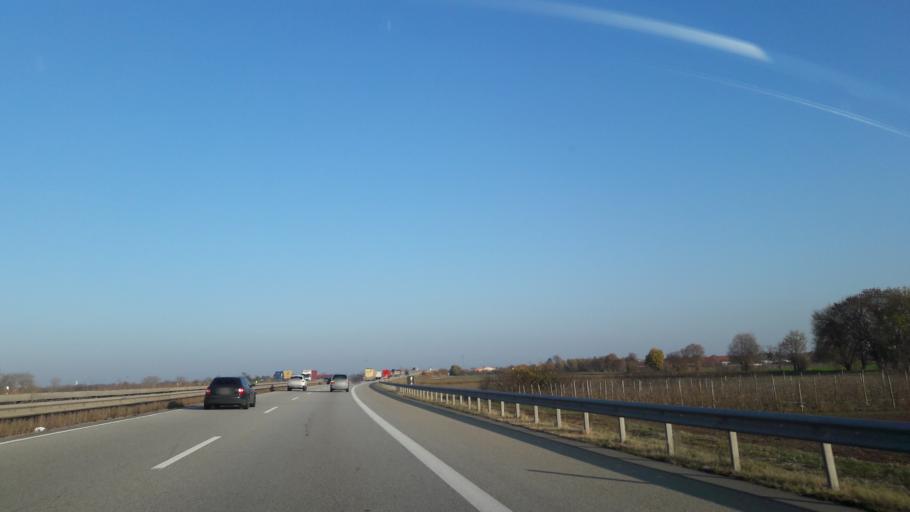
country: DE
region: Rheinland-Pfalz
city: Dirmstein
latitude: 49.5509
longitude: 8.2496
